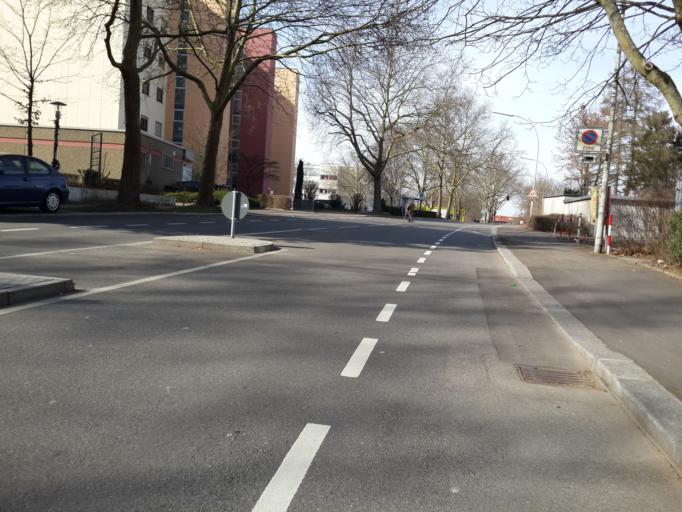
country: DE
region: Baden-Wuerttemberg
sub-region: Regierungsbezirk Stuttgart
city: Heilbronn
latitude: 49.1457
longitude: 9.1825
